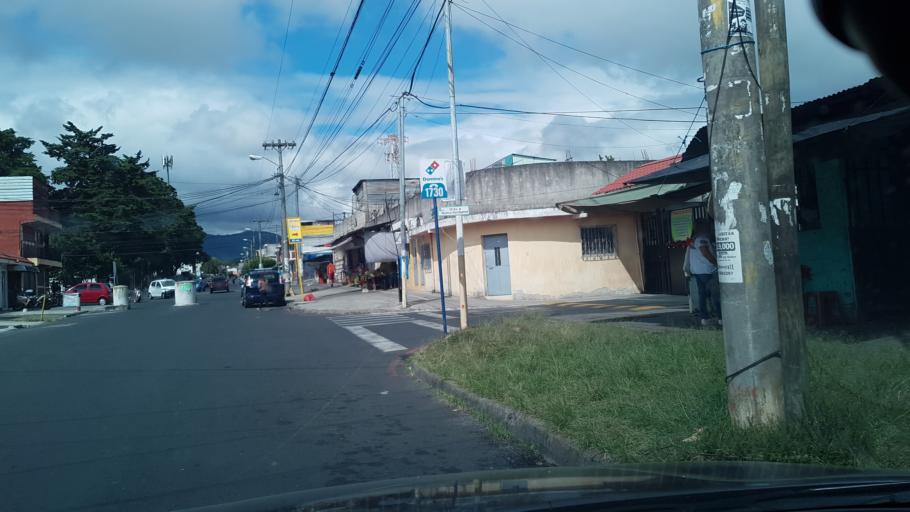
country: GT
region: Guatemala
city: Mixco
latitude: 14.6408
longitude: -90.5752
